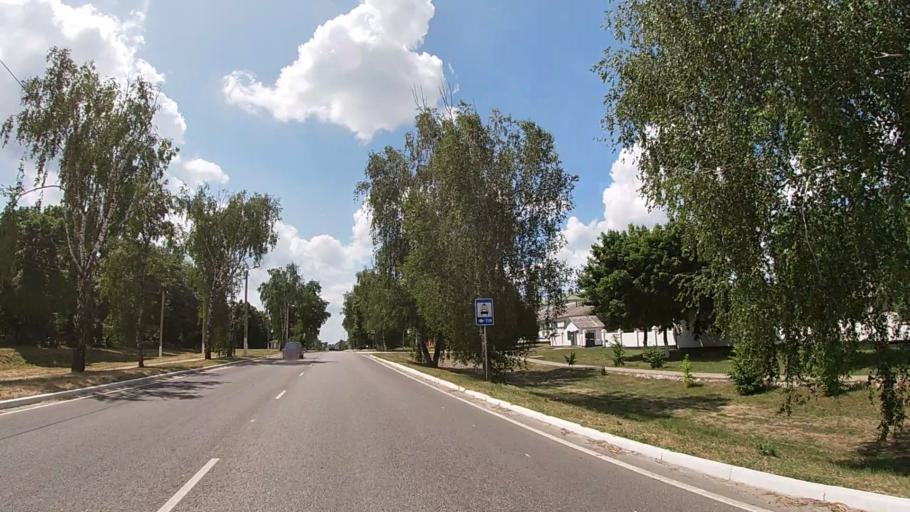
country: RU
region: Belgorod
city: Grayvoron
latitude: 50.4869
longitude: 35.6909
